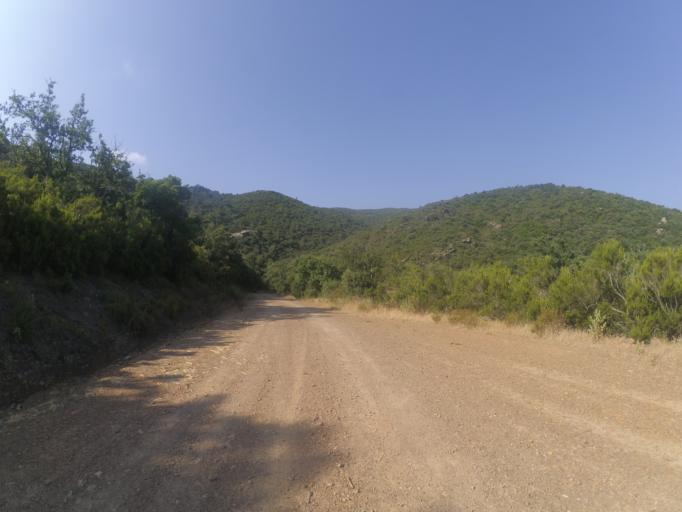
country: FR
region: Languedoc-Roussillon
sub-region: Departement des Pyrenees-Orientales
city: Ille-sur-Tet
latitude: 42.6508
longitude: 2.6503
